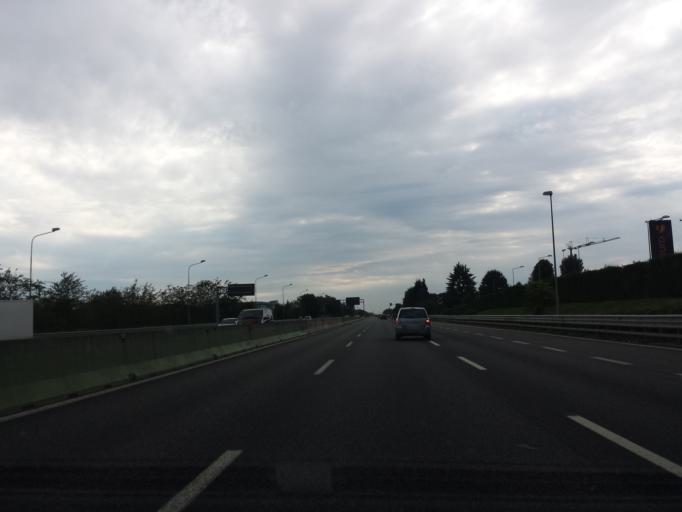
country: IT
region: Lombardy
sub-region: Citta metropolitana di Milano
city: Cerro Maggiore
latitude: 45.6016
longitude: 8.9485
